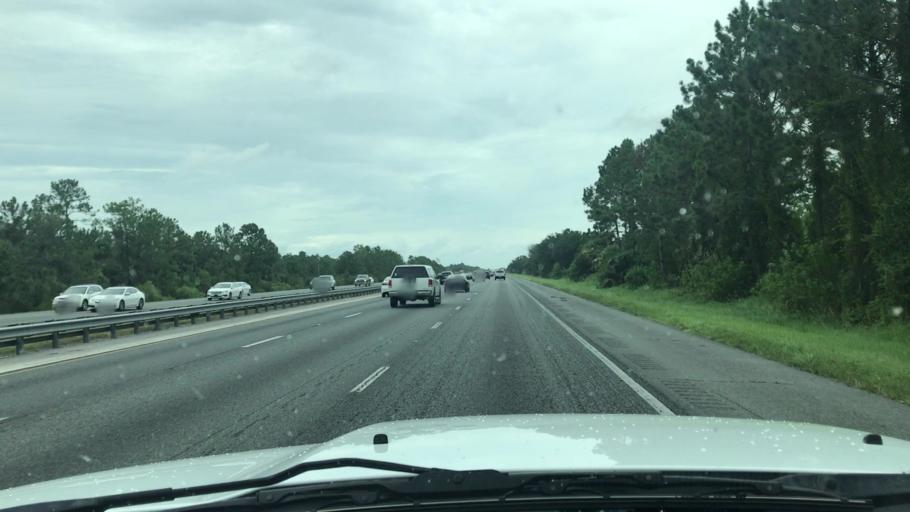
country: US
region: Florida
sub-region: Volusia County
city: Ormond-by-the-Sea
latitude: 29.3086
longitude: -81.1315
